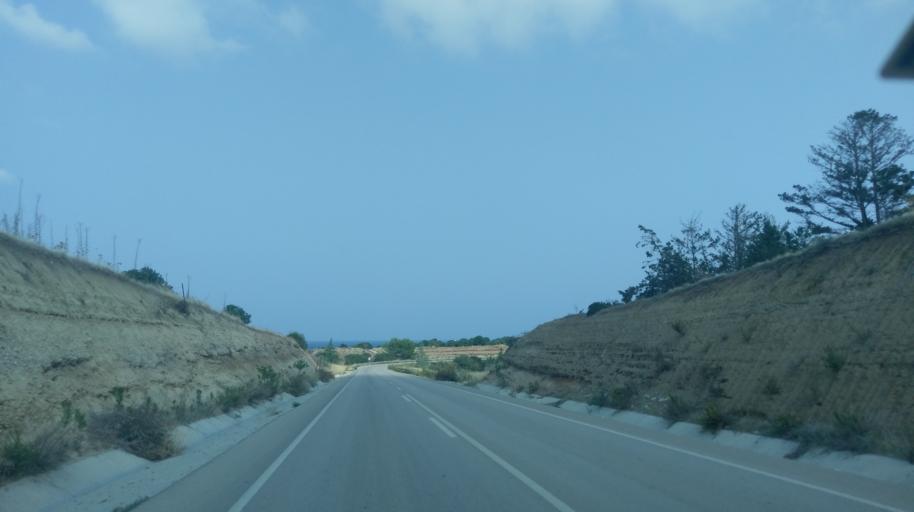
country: CY
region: Ammochostos
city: Lefkonoiko
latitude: 35.3985
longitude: 33.7600
